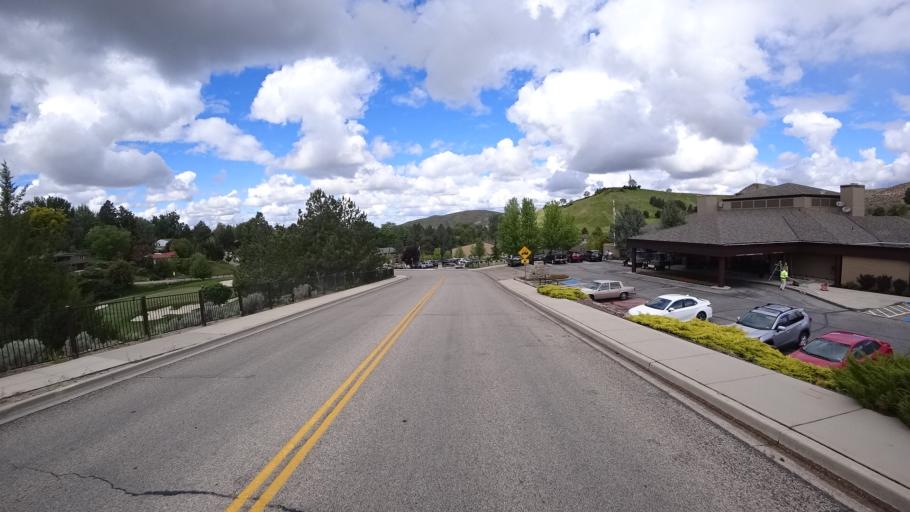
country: US
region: Idaho
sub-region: Ada County
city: Boise
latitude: 43.6487
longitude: -116.1908
